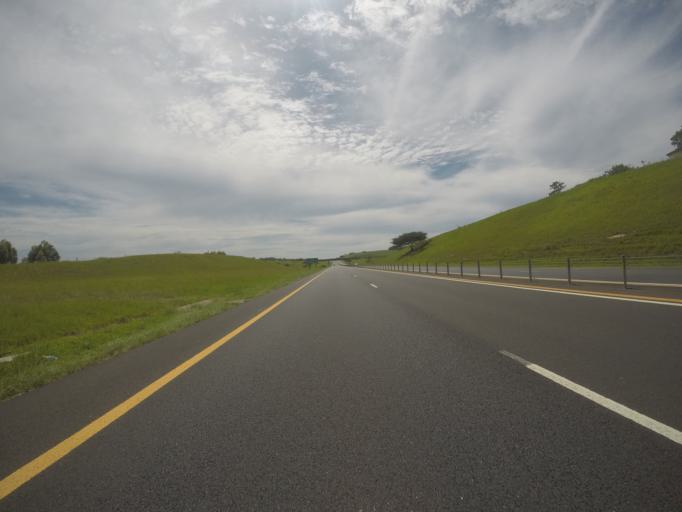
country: ZA
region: KwaZulu-Natal
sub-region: iLembe District Municipality
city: Mandeni
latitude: -29.1797
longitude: 31.4979
